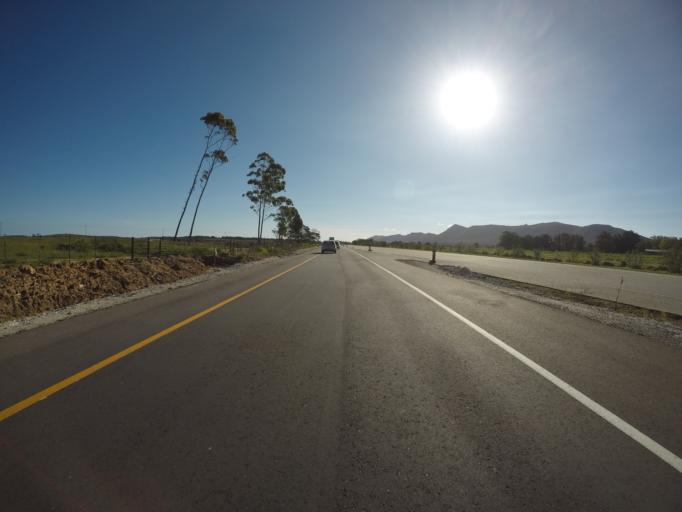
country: ZA
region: Eastern Cape
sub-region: Nelson Mandela Bay Metropolitan Municipality
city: Uitenhage
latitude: -33.9190
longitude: 25.2920
